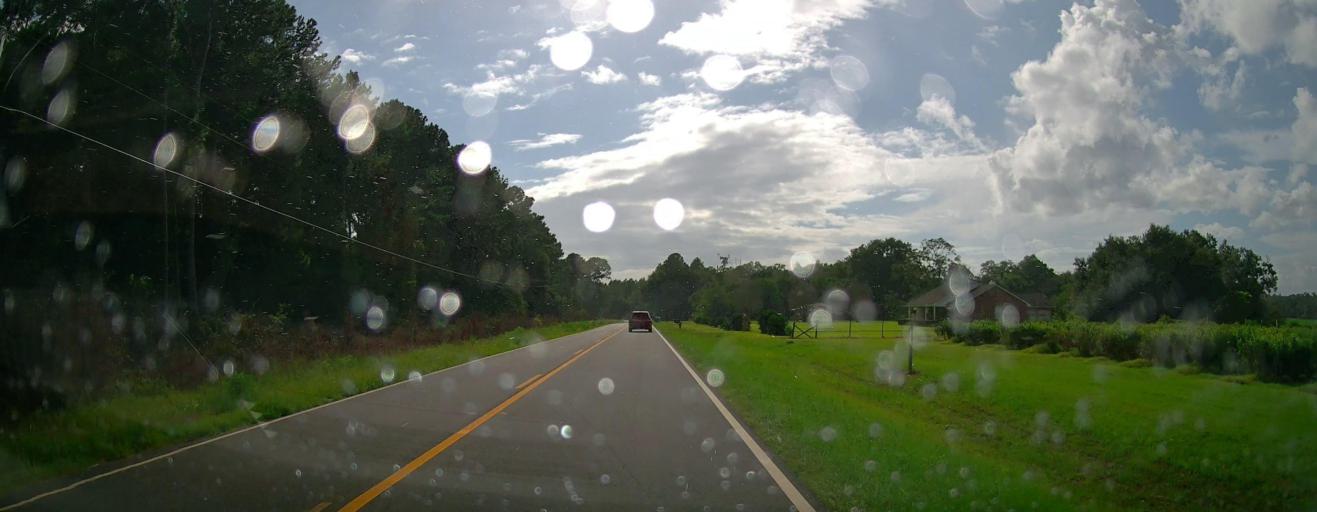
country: US
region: Georgia
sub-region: Coffee County
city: Douglas
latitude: 31.4540
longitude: -82.8559
